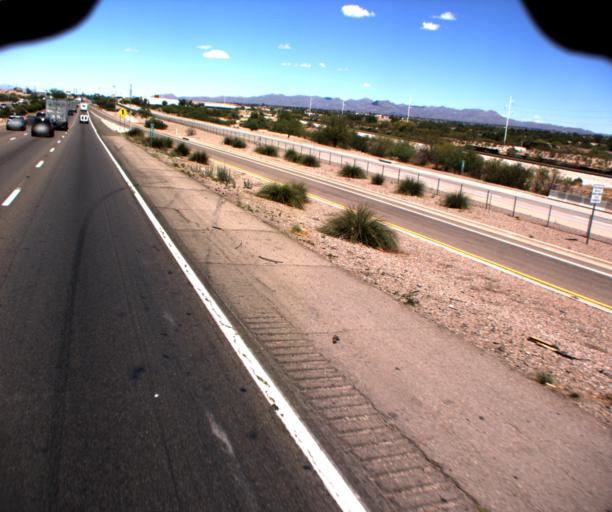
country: US
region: Arizona
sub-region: Pima County
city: Flowing Wells
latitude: 32.3111
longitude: -111.0430
